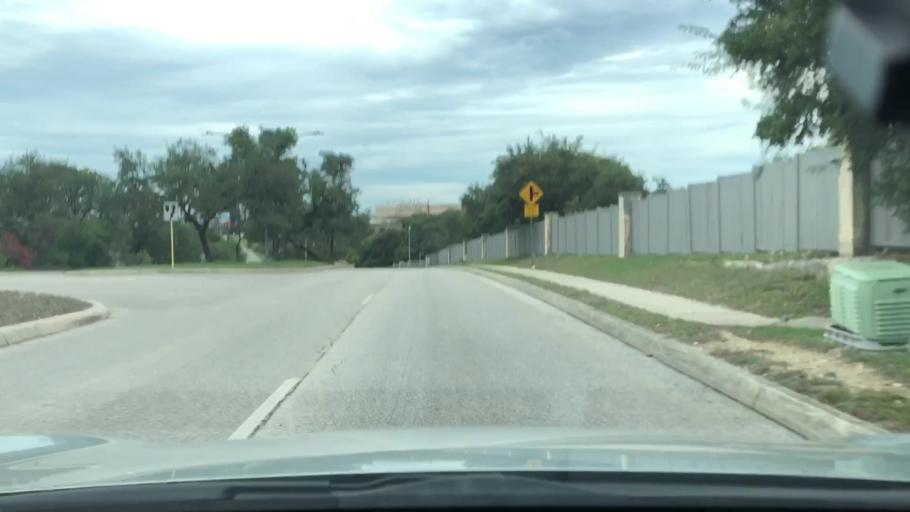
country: US
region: Texas
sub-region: Bexar County
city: Leon Valley
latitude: 29.4648
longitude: -98.6741
